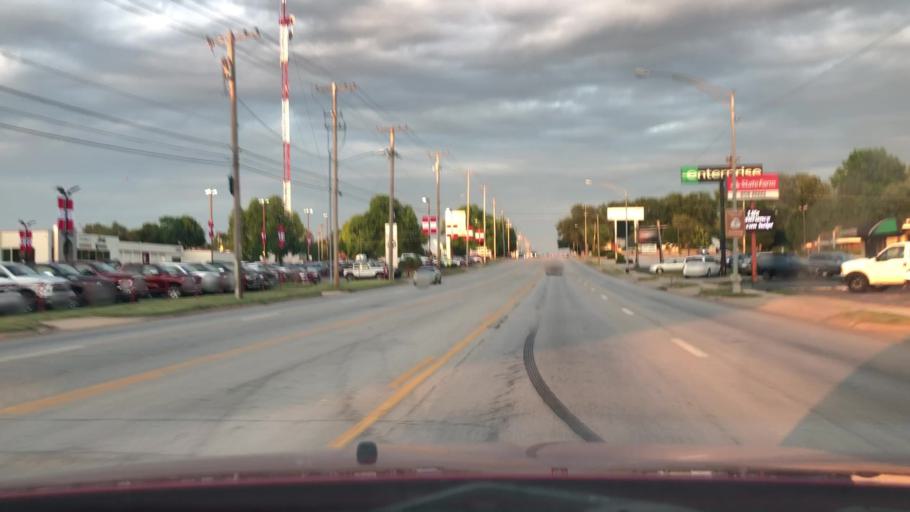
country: US
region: Missouri
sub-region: Greene County
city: Springfield
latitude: 37.1823
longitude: -93.3065
